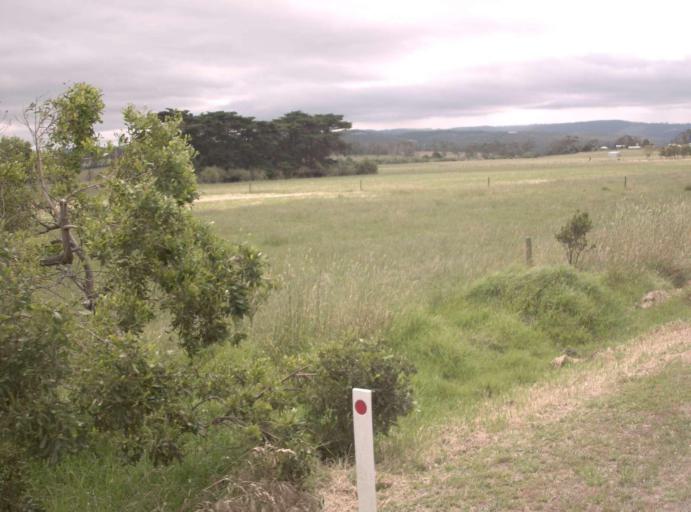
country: AU
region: Victoria
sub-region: Latrobe
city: Traralgon
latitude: -38.5511
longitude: 146.6544
